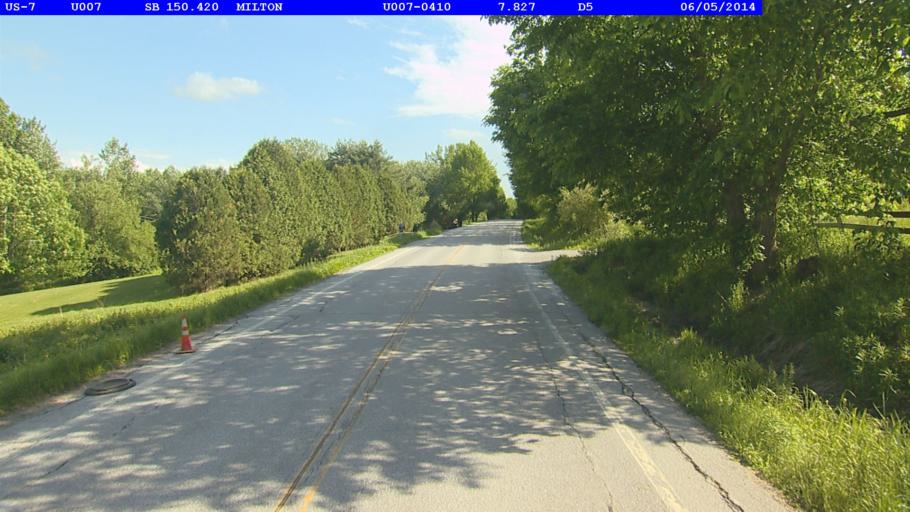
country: US
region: Vermont
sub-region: Chittenden County
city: Milton
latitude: 44.6791
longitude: -73.1110
